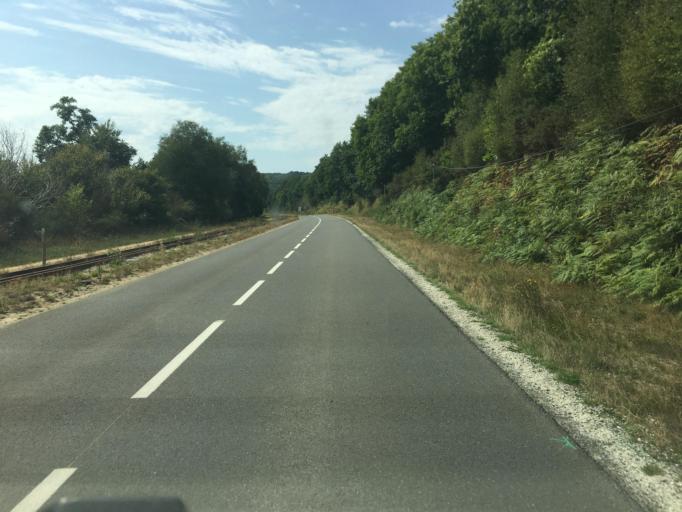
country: FR
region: Brittany
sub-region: Departement des Cotes-d'Armor
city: Gouarec
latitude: 48.2152
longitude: -3.1434
